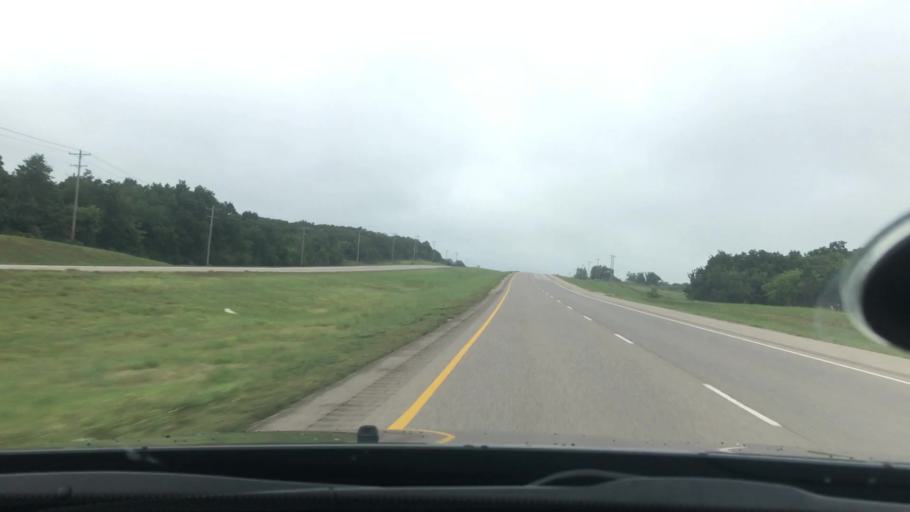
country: US
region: Oklahoma
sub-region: Seminole County
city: Seminole
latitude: 35.3278
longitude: -96.6713
